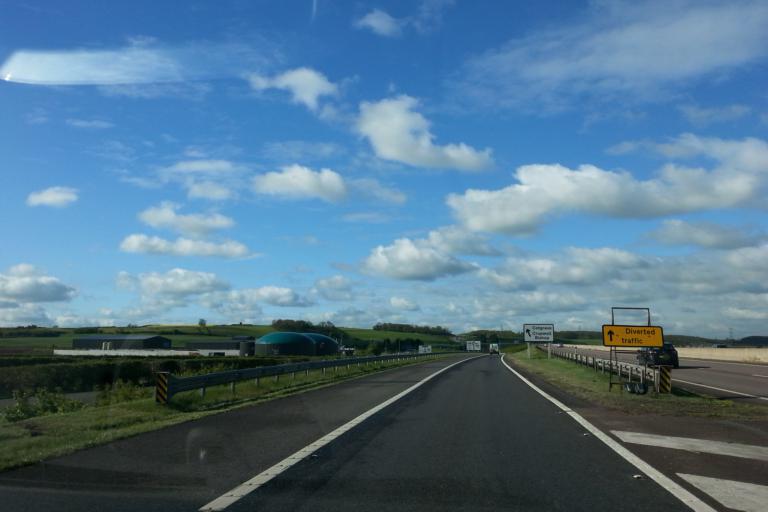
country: GB
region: England
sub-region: Nottinghamshire
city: Cropwell Bishop
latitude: 52.9219
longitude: -1.0054
